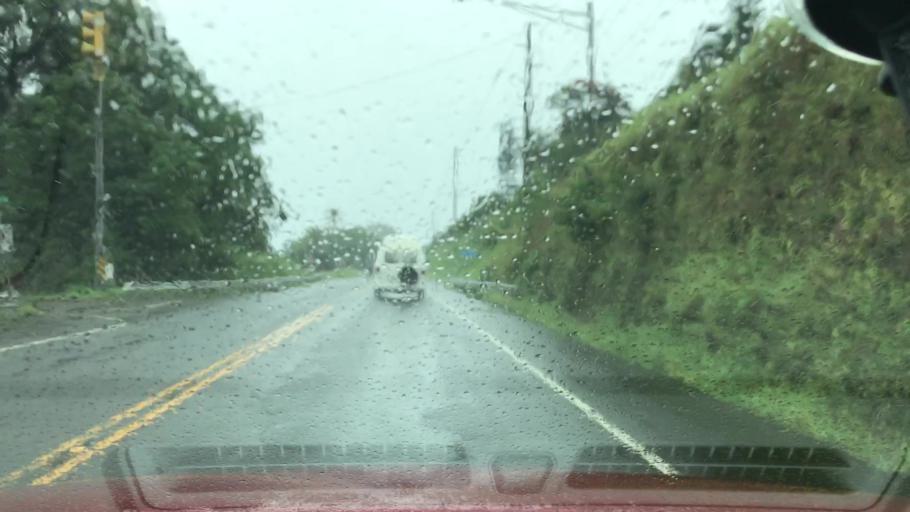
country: US
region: Hawaii
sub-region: Hawaii County
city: Pepeekeo
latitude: 19.9854
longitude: -155.2376
